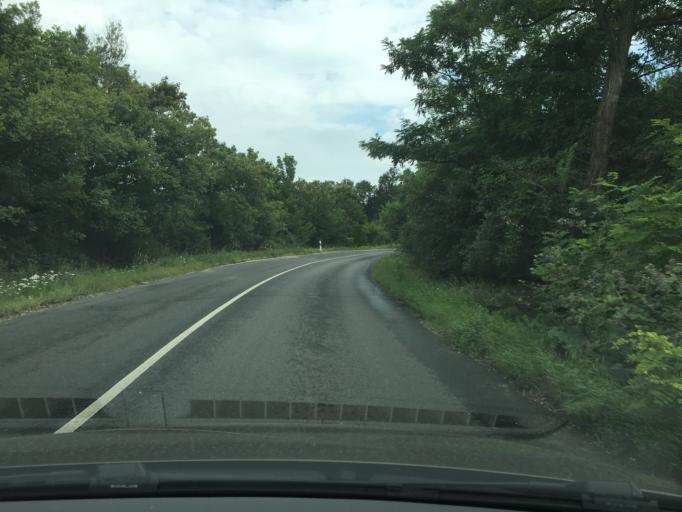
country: HU
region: Pest
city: Toeroekbalint
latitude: 47.4256
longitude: 18.8934
